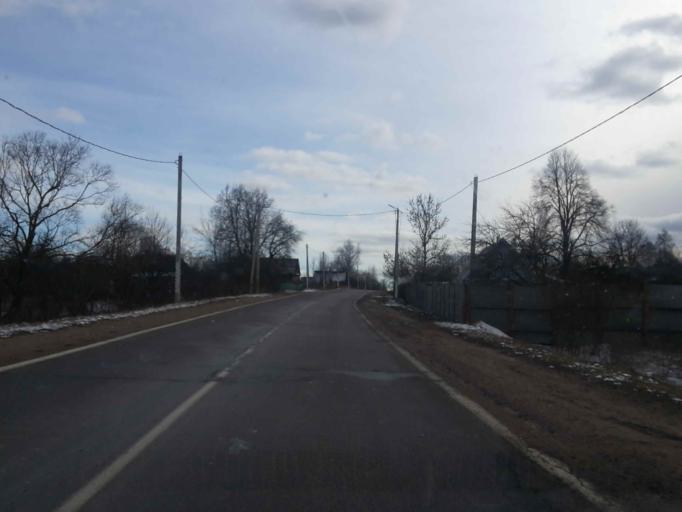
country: BY
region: Vitebsk
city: Pastavy
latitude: 55.0072
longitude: 26.8828
